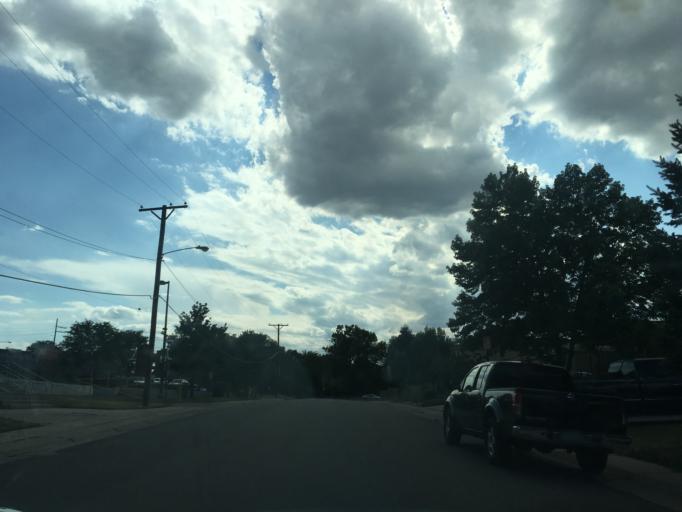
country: US
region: Colorado
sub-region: Jefferson County
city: Lakewood
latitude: 39.6838
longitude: -105.0514
